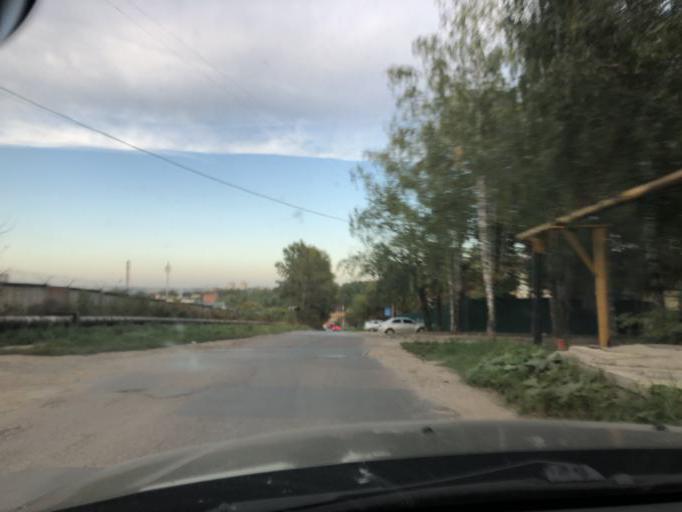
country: RU
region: Tula
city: Mendeleyevskiy
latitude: 54.1581
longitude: 37.6121
